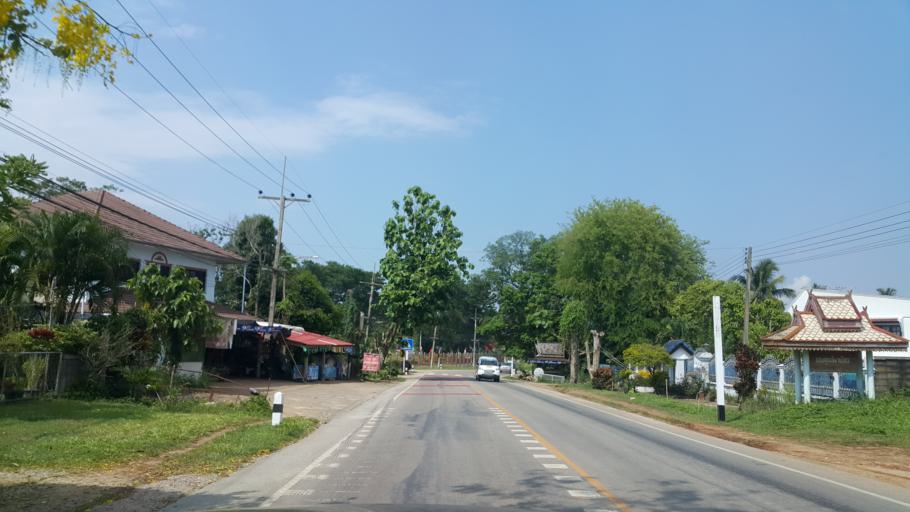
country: TH
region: Chiang Rai
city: Wiang Chiang Rung
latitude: 20.0137
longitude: 99.9272
